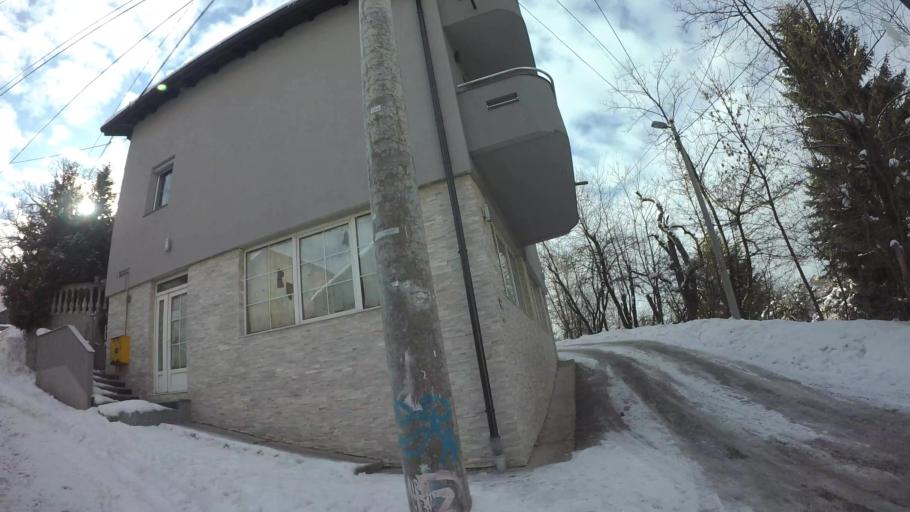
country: BA
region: Federation of Bosnia and Herzegovina
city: Kobilja Glava
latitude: 43.8807
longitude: 18.4168
